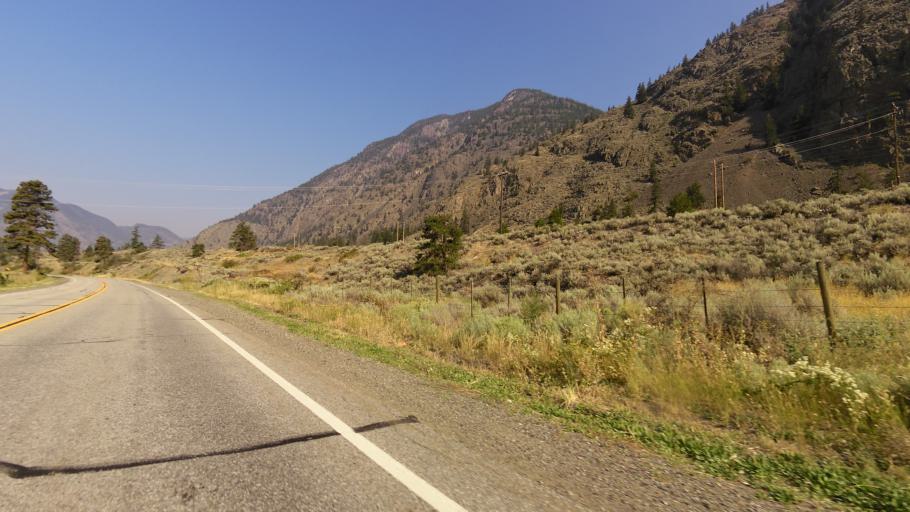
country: CA
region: British Columbia
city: Oliver
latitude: 49.2180
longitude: -119.9206
